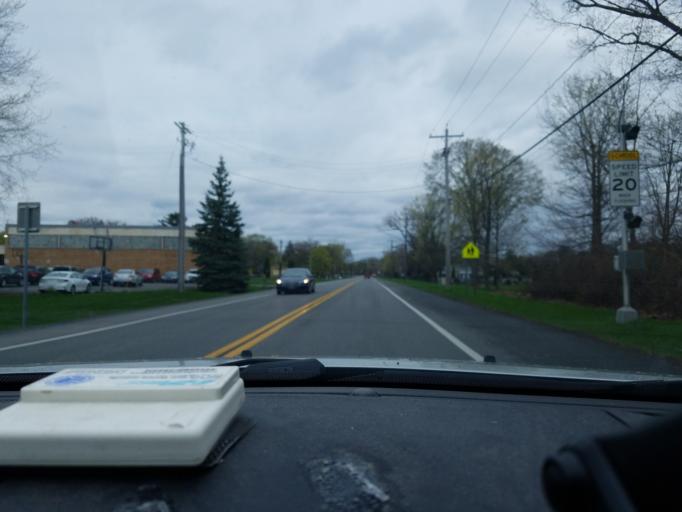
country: US
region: New York
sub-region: Onondaga County
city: North Syracuse
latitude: 43.1296
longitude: -76.1315
